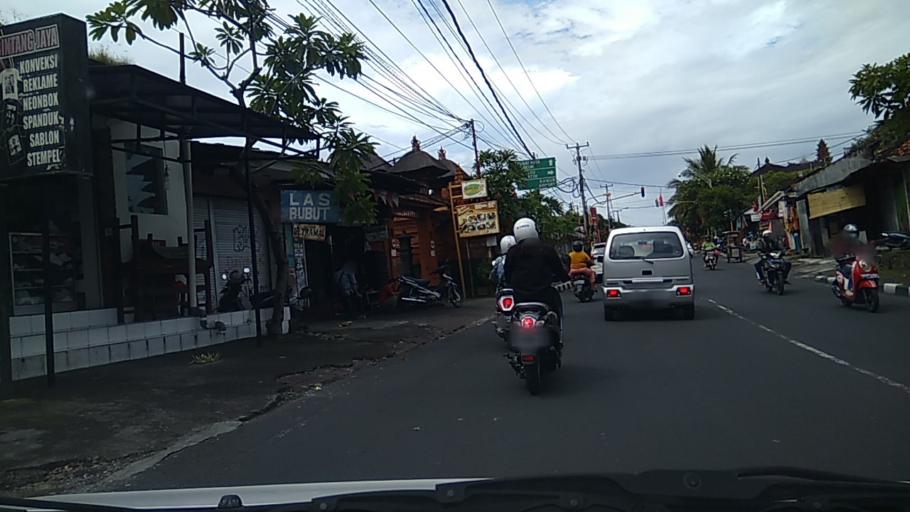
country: ID
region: Bali
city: Dajan Tangluk
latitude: -8.6461
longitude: 115.2458
